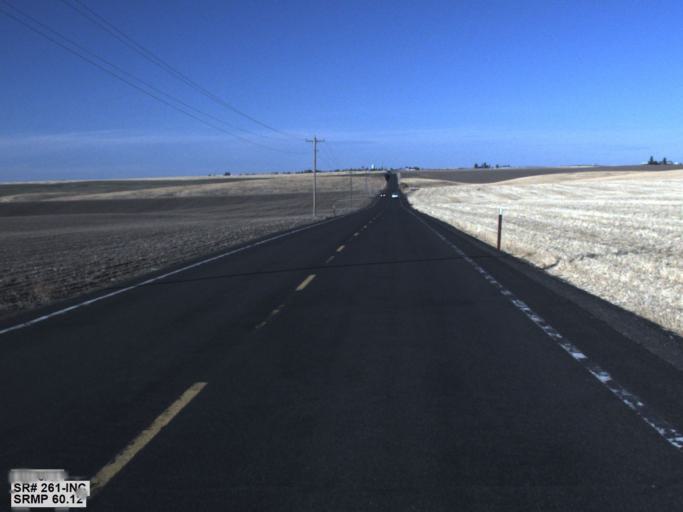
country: US
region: Washington
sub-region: Adams County
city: Ritzville
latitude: 47.0779
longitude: -118.3654
